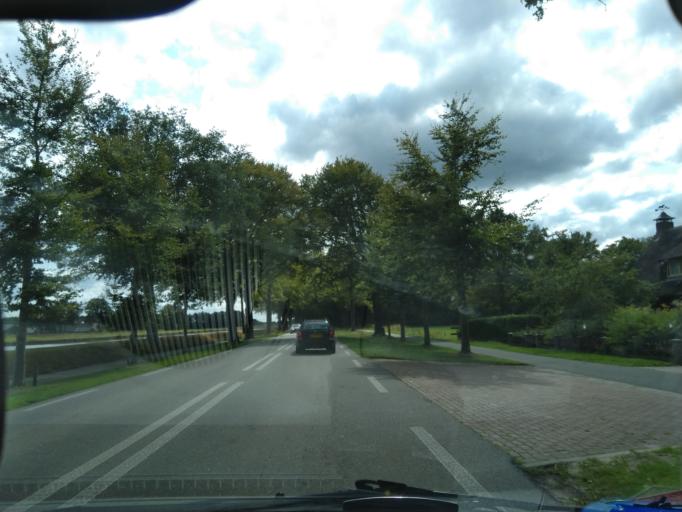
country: NL
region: Drenthe
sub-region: Gemeente Tynaarlo
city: Tynaarlo
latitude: 53.1089
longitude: 6.6044
